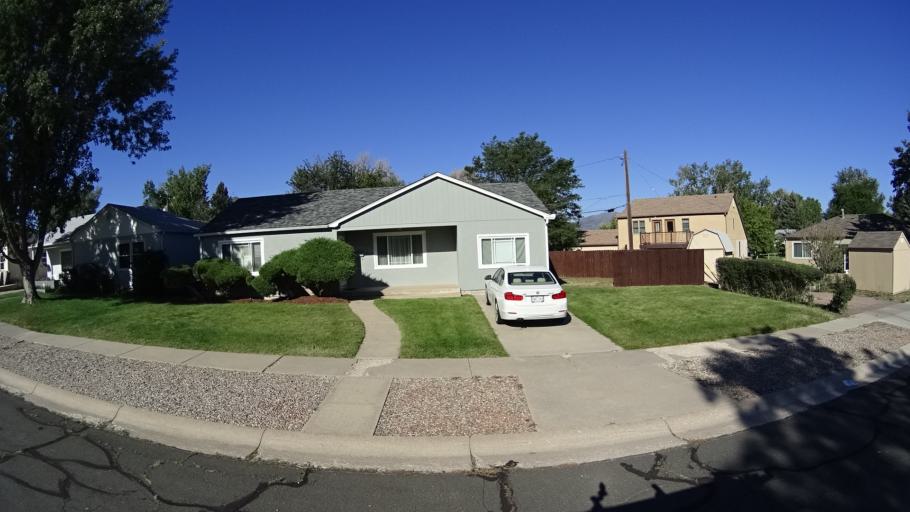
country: US
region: Colorado
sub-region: El Paso County
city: Colorado Springs
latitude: 38.8654
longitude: -104.7974
